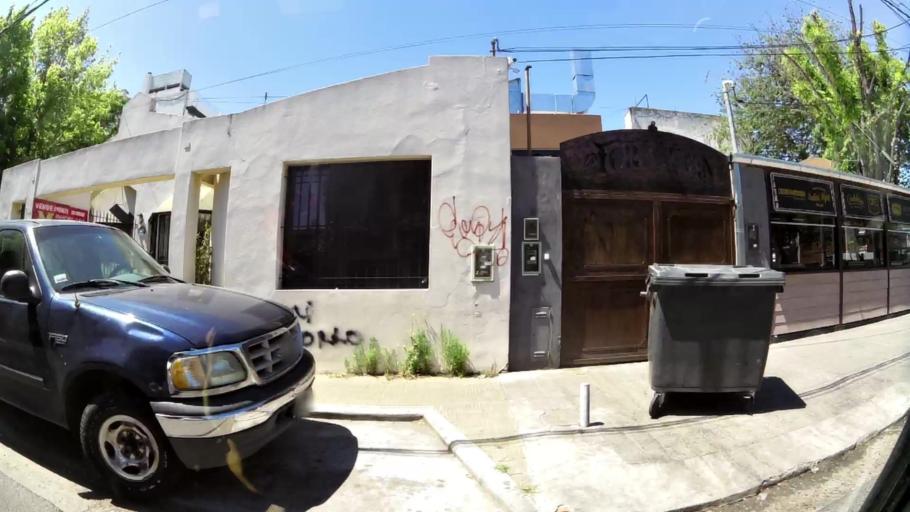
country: AR
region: Buenos Aires
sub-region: Partido de Vicente Lopez
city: Olivos
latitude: -34.5052
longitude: -58.4933
